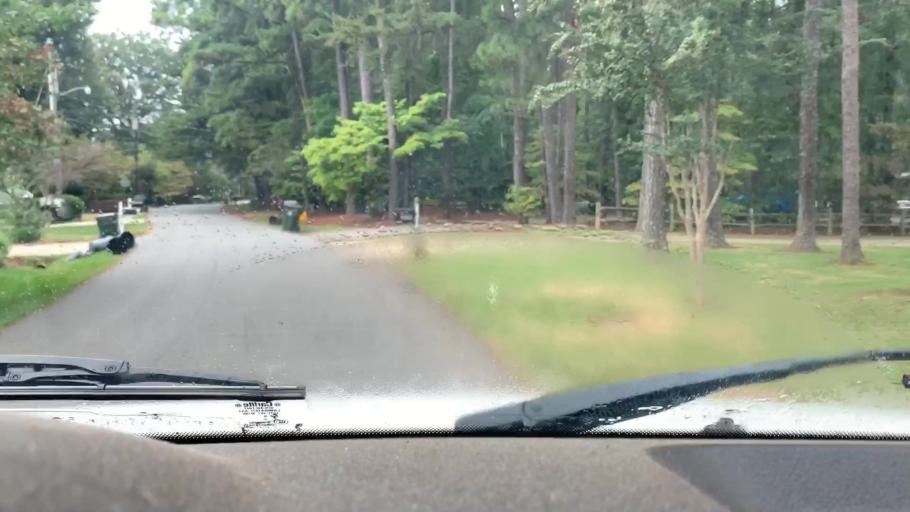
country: US
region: North Carolina
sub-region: Mecklenburg County
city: Cornelius
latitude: 35.4915
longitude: -80.9108
